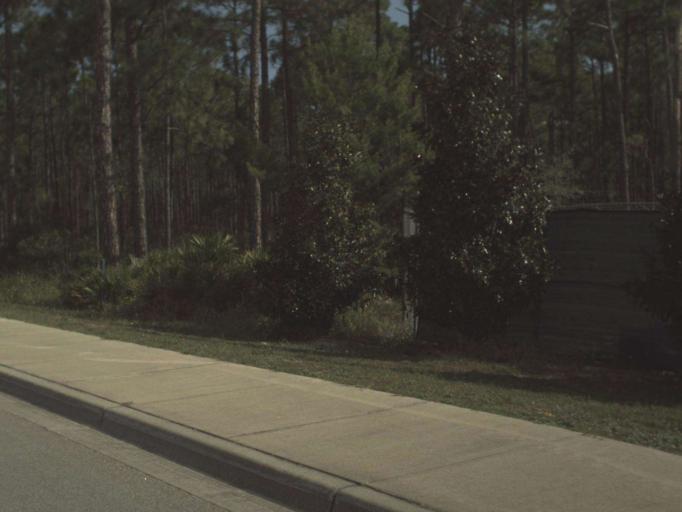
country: US
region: Florida
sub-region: Walton County
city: Seaside
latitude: 30.3742
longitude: -86.1797
